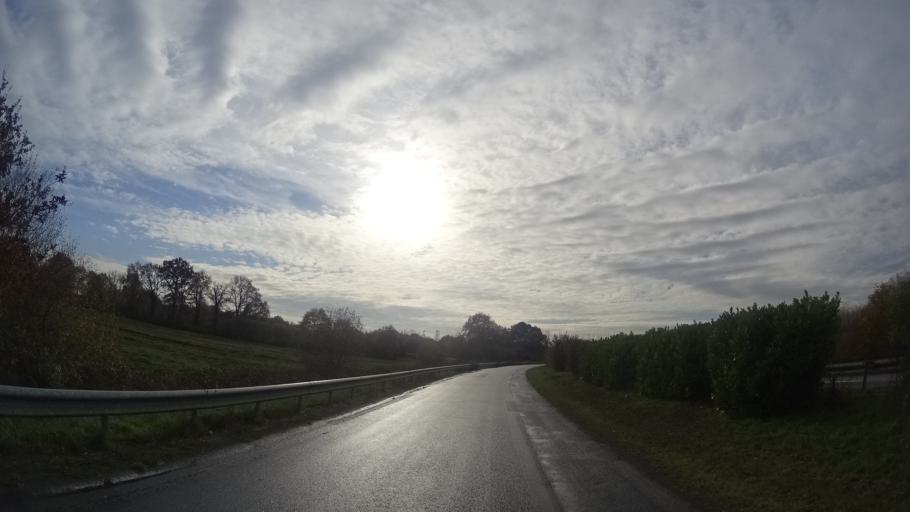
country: FR
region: Brittany
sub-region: Departement du Morbihan
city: Rieux
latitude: 47.6223
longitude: -2.1018
